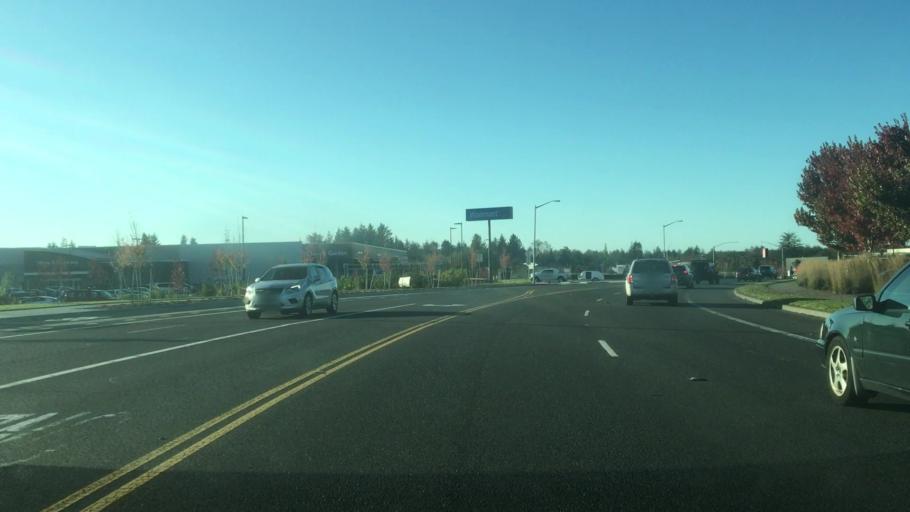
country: US
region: Oregon
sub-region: Clatsop County
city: Warrenton
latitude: 46.1453
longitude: -123.9147
